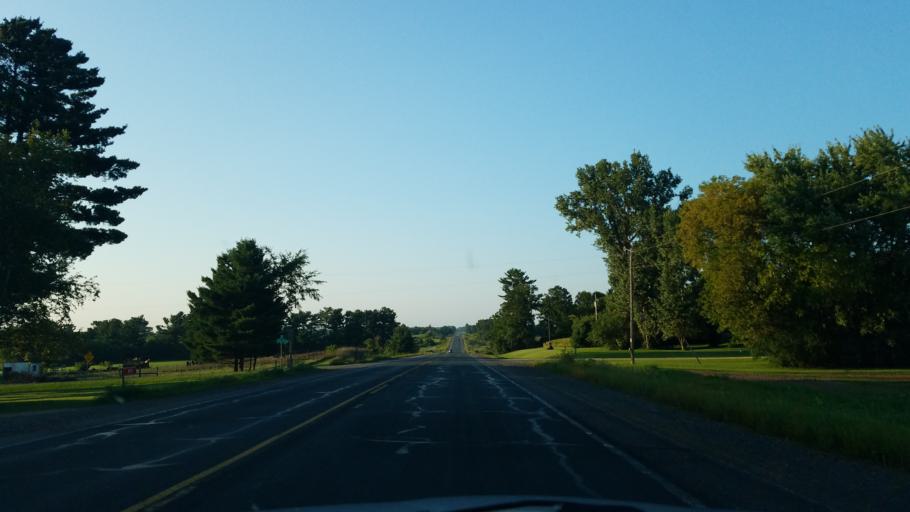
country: US
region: Wisconsin
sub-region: Polk County
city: Clear Lake
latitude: 45.2160
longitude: -92.2842
